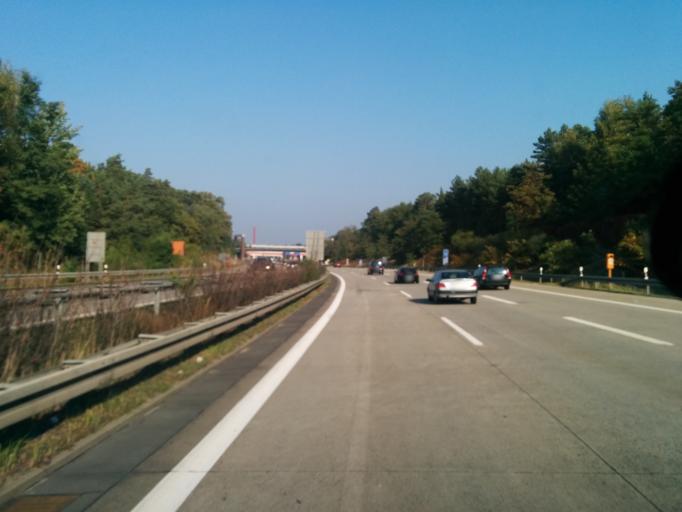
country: DE
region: Berlin
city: Nikolassee
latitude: 52.4128
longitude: 13.1975
